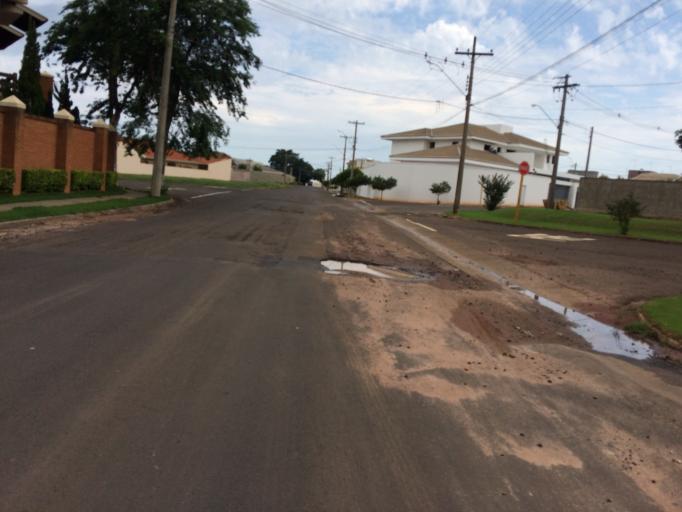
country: BR
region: Sao Paulo
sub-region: Matao
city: Matao
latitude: -21.6184
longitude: -48.3648
